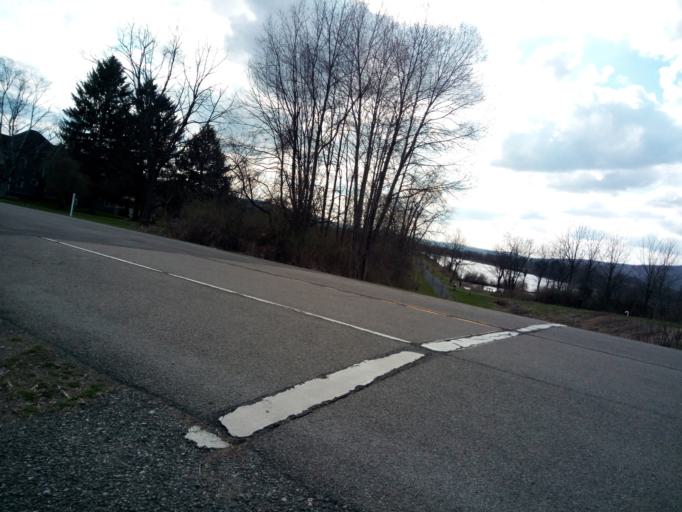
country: US
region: New York
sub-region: Chemung County
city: Big Flats
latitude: 42.1452
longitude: -76.9095
